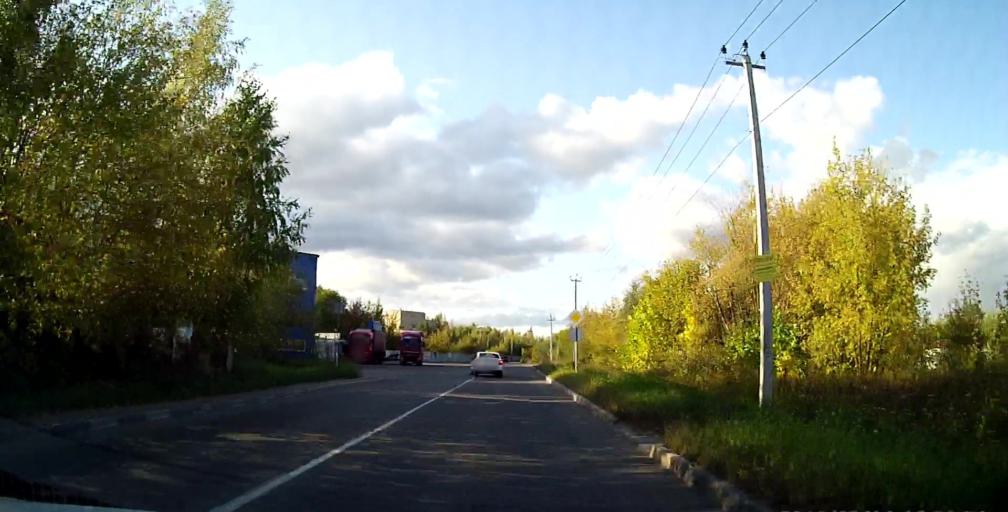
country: RU
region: Moskovskaya
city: Klimovsk
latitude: 55.3751
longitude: 37.5637
